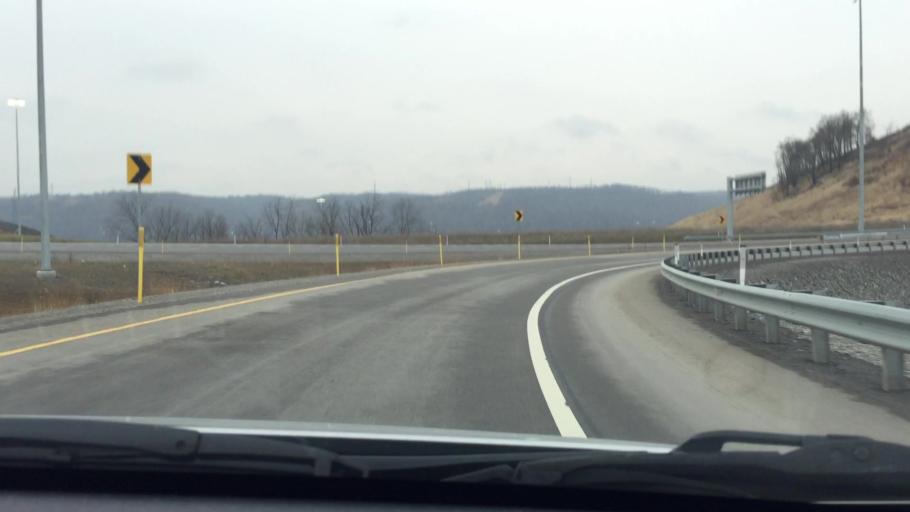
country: US
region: Pennsylvania
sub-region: Beaver County
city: Beaver
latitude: 40.6687
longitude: -80.3270
